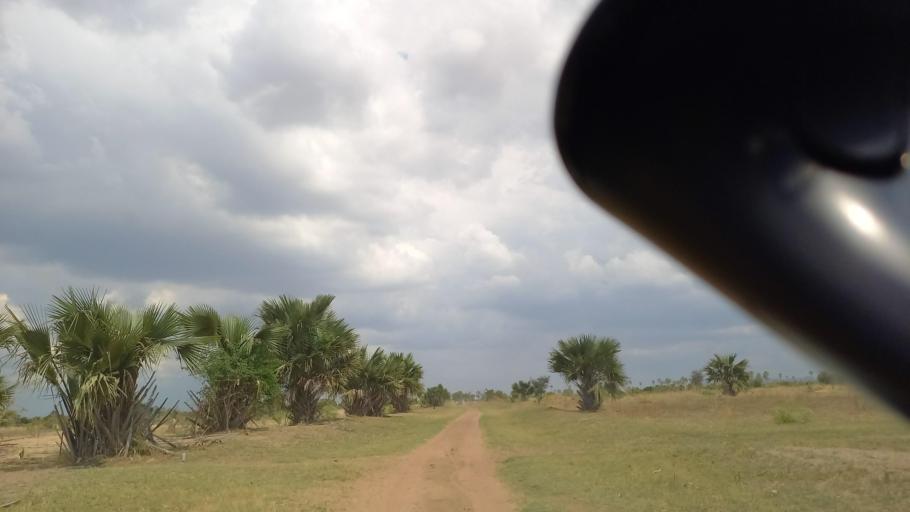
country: ZM
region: Lusaka
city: Kafue
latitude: -15.8292
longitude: 28.0596
